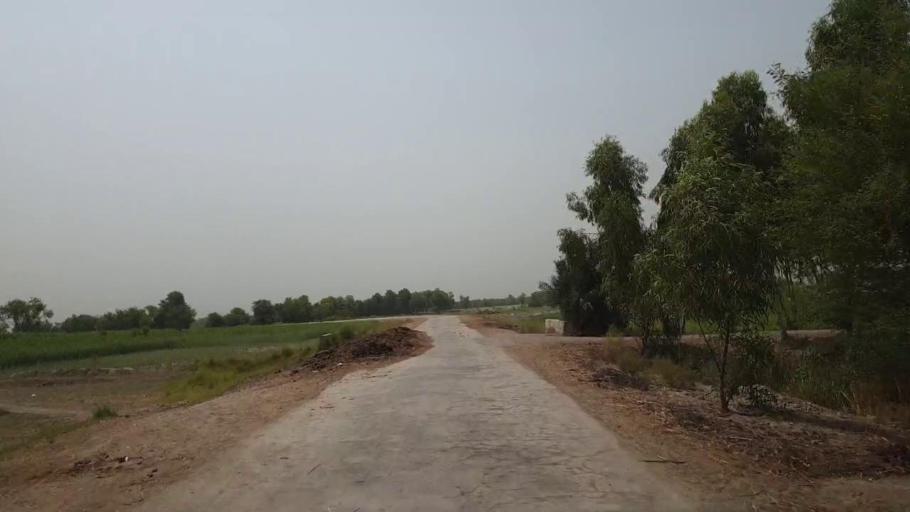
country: PK
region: Sindh
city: Gambat
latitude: 27.4440
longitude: 68.5152
